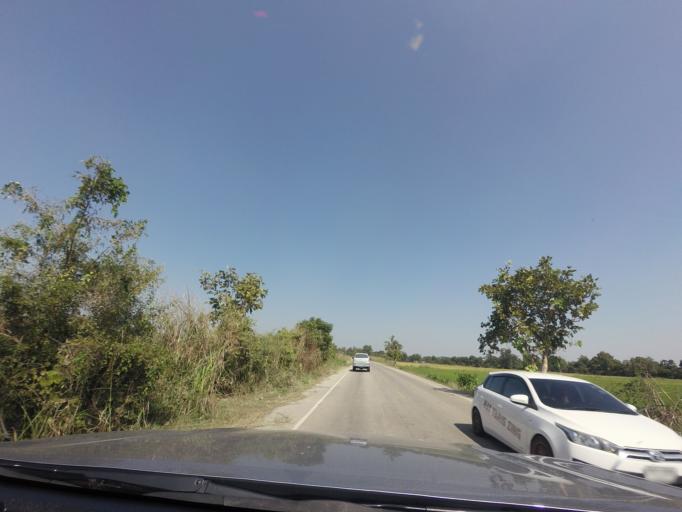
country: TH
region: Sukhothai
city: Si Samrong
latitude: 17.1166
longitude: 99.7788
